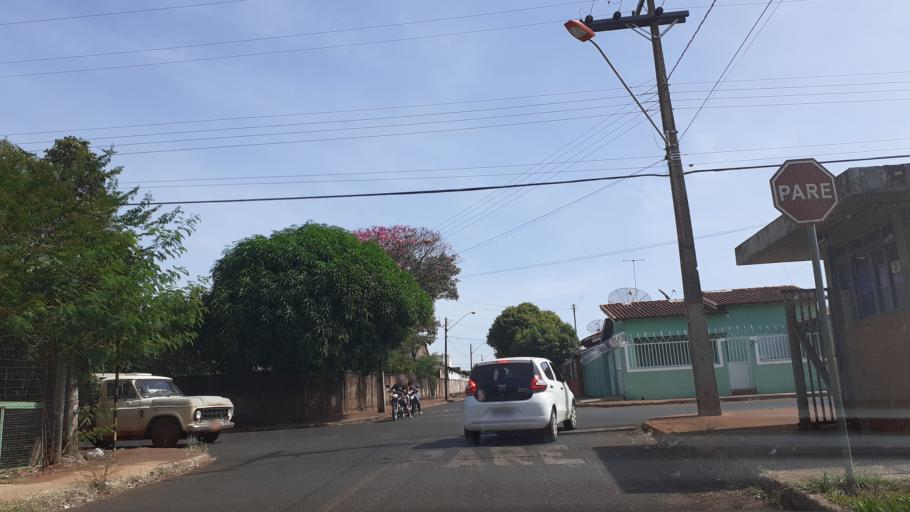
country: BR
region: Goias
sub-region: Itumbiara
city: Itumbiara
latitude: -18.4152
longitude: -49.2312
